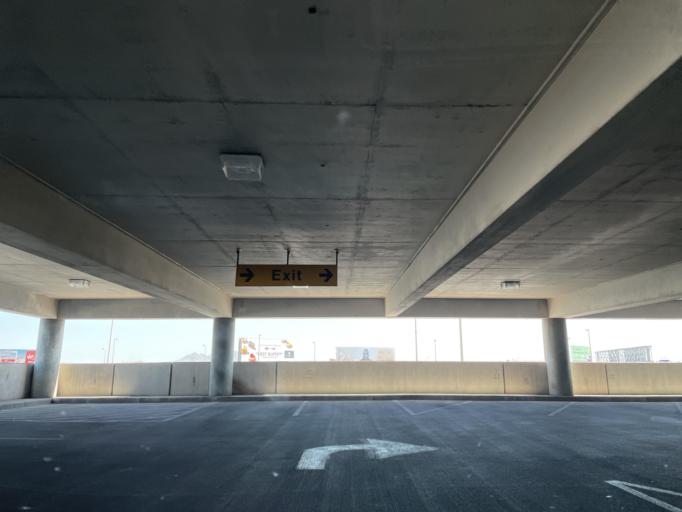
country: US
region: Nevada
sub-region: Clark County
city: Paradise
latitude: 36.0873
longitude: -115.1477
